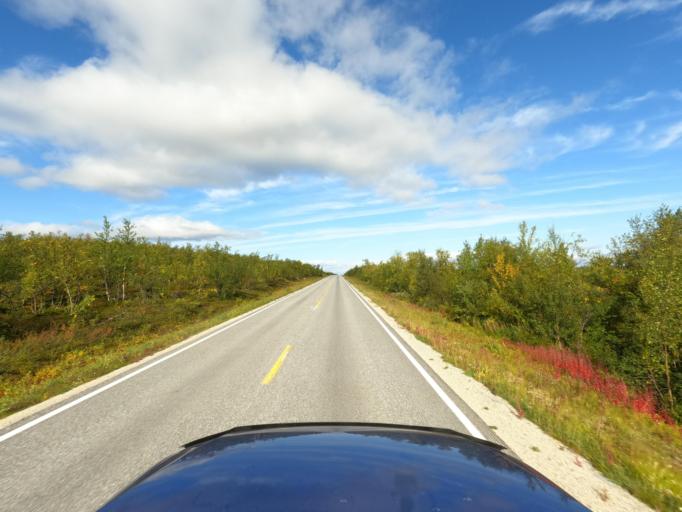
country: NO
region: Finnmark Fylke
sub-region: Karasjok
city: Karasjohka
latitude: 69.6507
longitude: 25.2794
